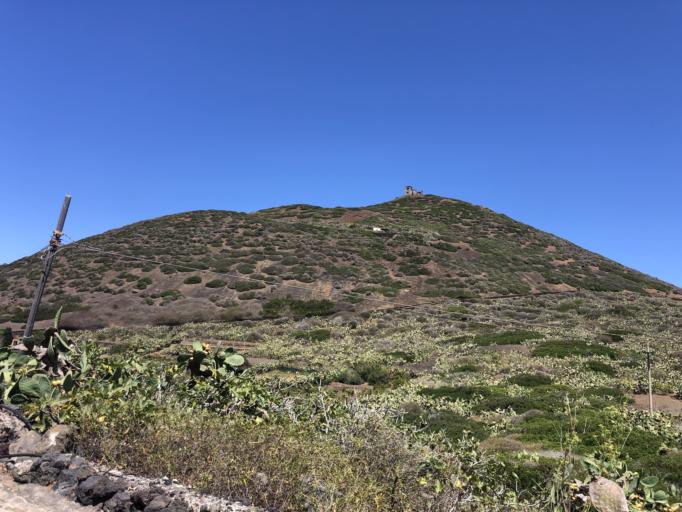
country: IT
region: Sicily
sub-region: Agrigento
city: Lampedusa
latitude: 35.8640
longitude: 12.8715
